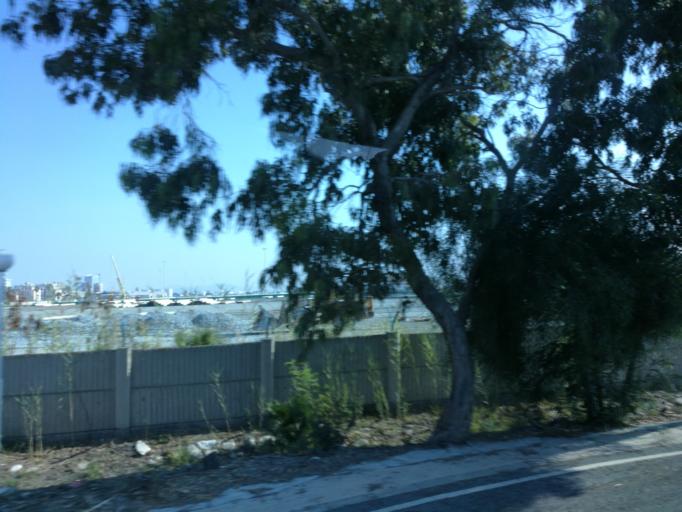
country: CY
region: Larnaka
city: Larnaca
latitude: 34.9187
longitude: 33.6388
